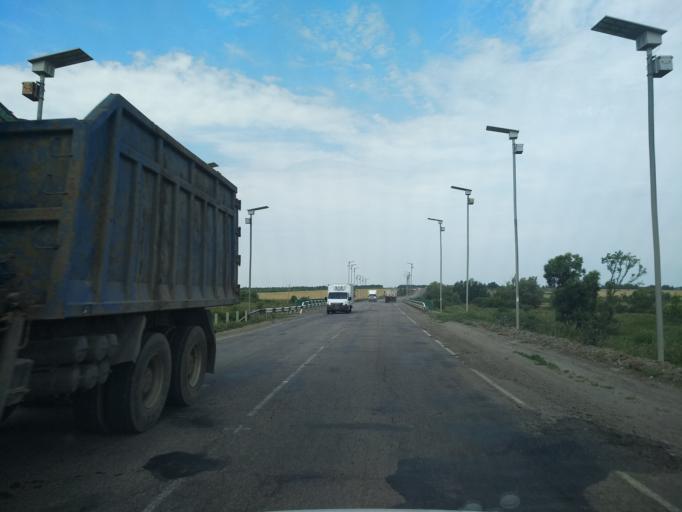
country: RU
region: Voronezj
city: Verkhnyaya Khava
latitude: 51.6746
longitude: 39.8204
